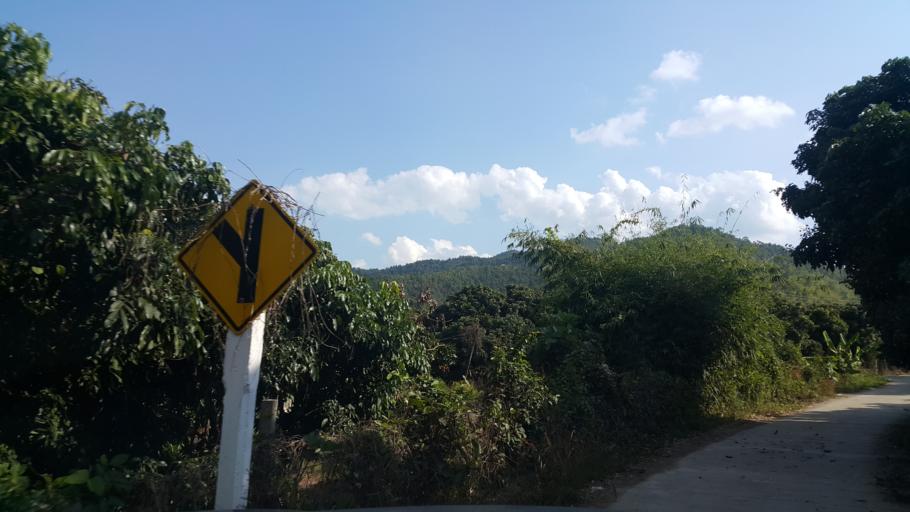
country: TH
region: Lamphun
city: Ban Thi
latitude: 18.5694
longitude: 99.1273
